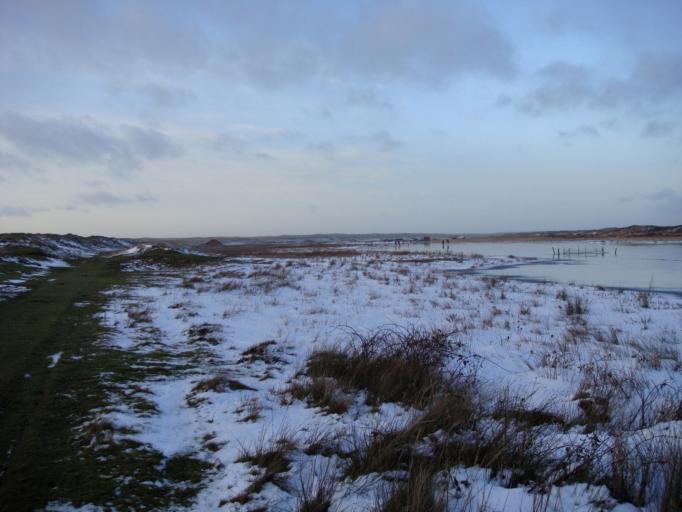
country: NL
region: North Holland
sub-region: Gemeente Den Helder
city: Den Helder
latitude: 53.0213
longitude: 4.7192
